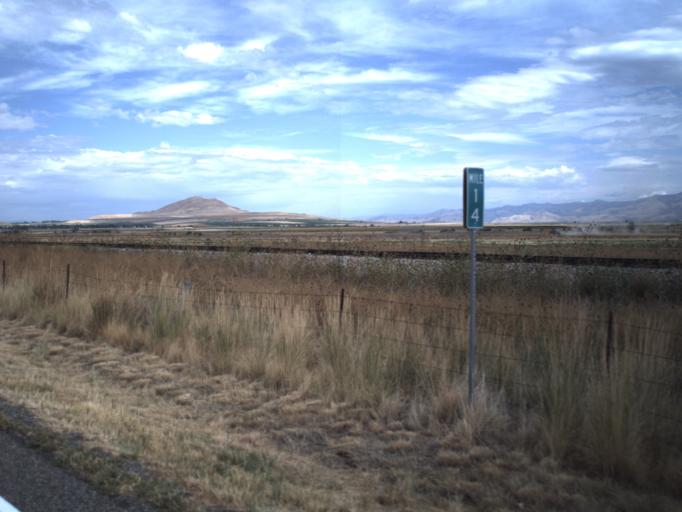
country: US
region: Utah
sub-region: Cache County
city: Benson
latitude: 41.8063
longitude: -111.9937
